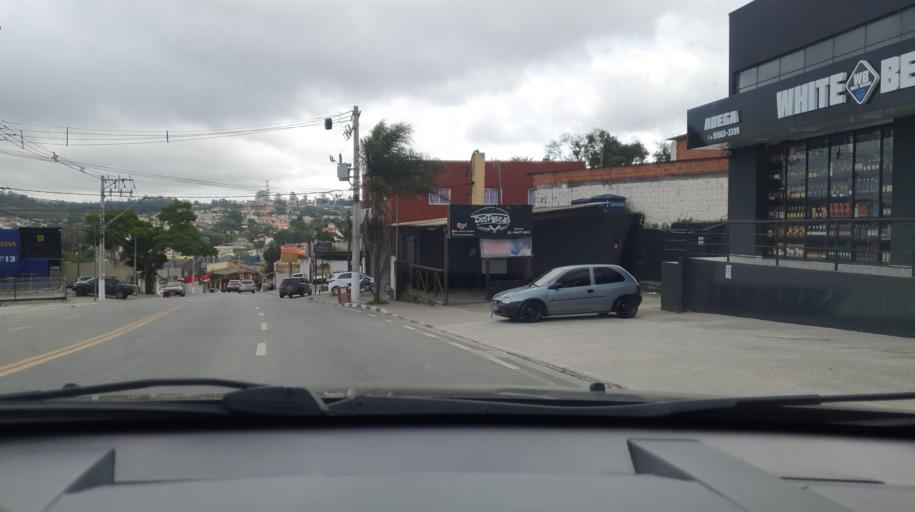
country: BR
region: Sao Paulo
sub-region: Vargem Grande Paulista
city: Vargem Grande Paulista
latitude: -23.6823
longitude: -47.0187
